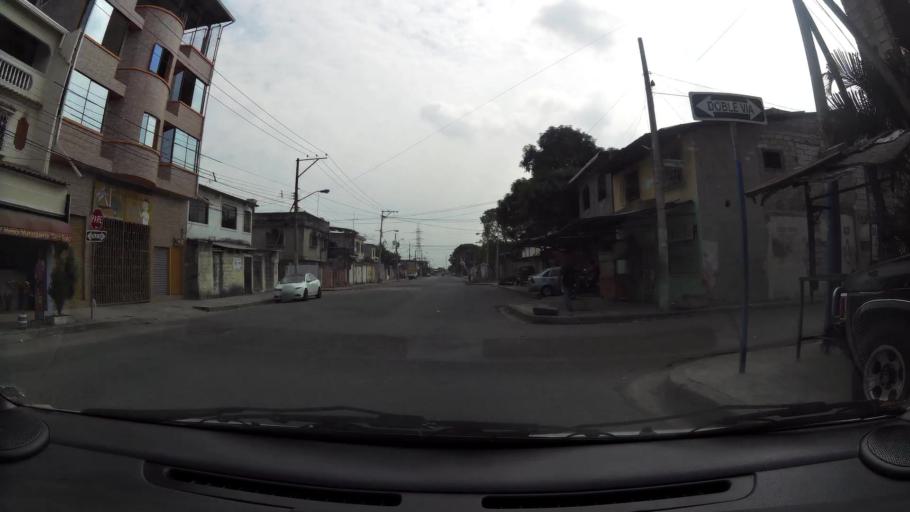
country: EC
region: Guayas
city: Guayaquil
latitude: -2.2408
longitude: -79.9073
